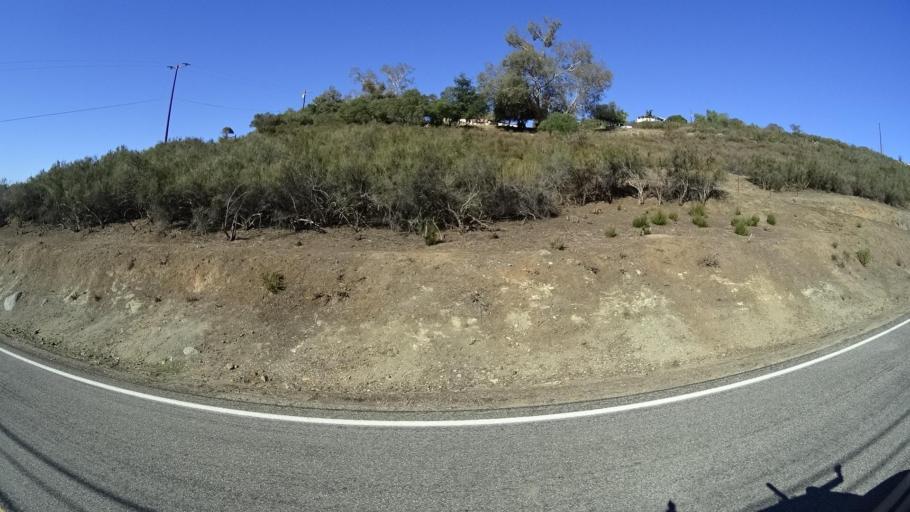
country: US
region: California
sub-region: San Diego County
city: Jamul
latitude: 32.6941
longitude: -116.7474
